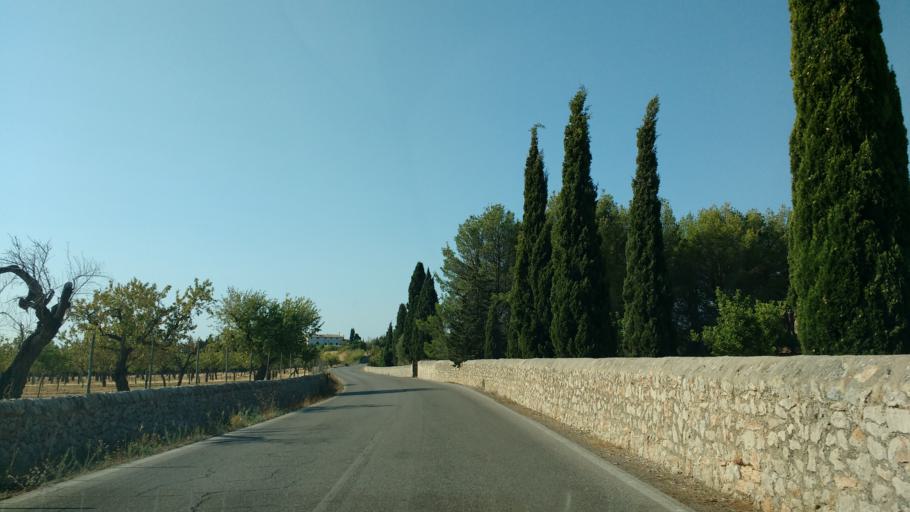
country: ES
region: Balearic Islands
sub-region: Illes Balears
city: Consell
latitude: 39.6789
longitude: 2.8130
